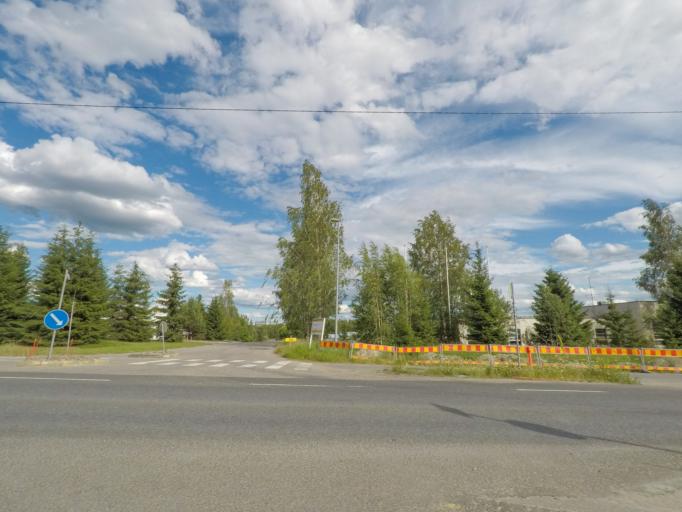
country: FI
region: Paijanne Tavastia
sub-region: Lahti
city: Lahti
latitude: 60.9563
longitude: 25.6184
